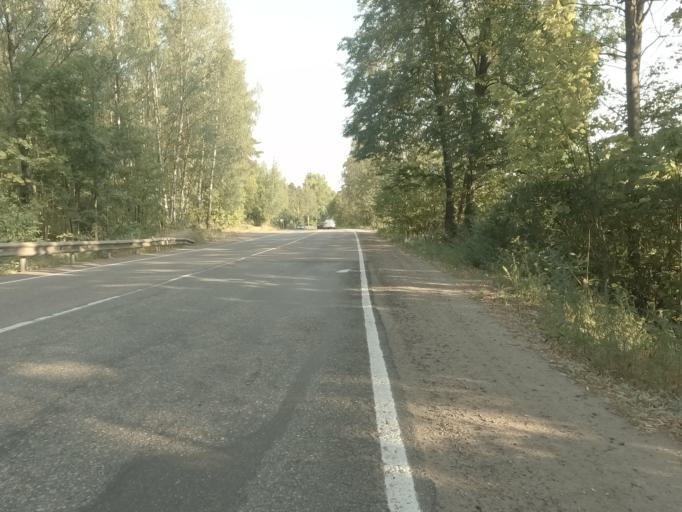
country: RU
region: Leningrad
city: Vyborg
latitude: 60.7334
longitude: 28.7585
